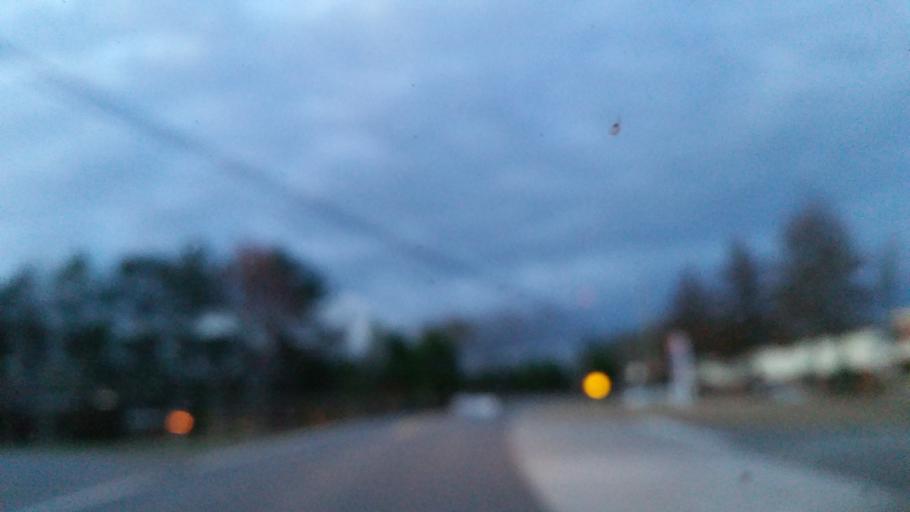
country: US
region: Georgia
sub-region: Cherokee County
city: Ball Ground
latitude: 34.3044
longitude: -84.4267
